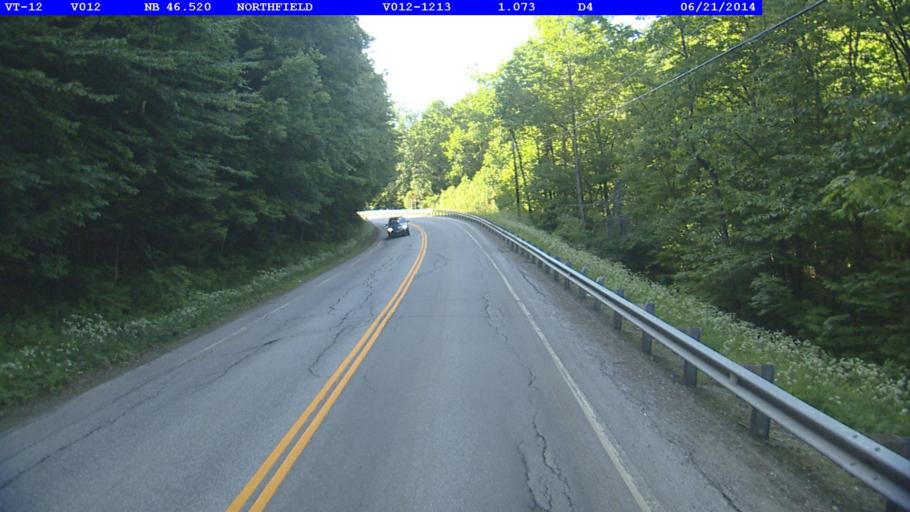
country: US
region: Vermont
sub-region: Washington County
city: Northfield
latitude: 44.1074
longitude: -72.6456
